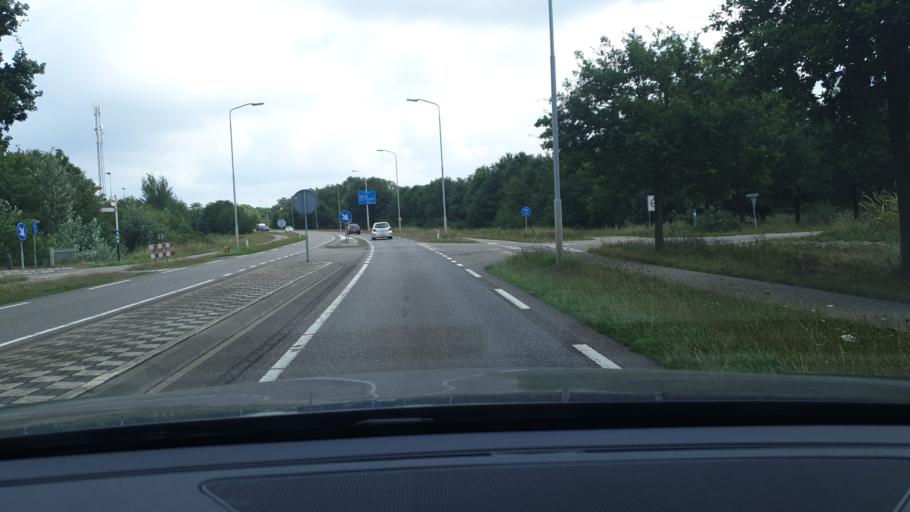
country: NL
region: North Brabant
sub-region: Gemeente Oirschot
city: Oirschot
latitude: 51.4919
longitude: 5.3024
